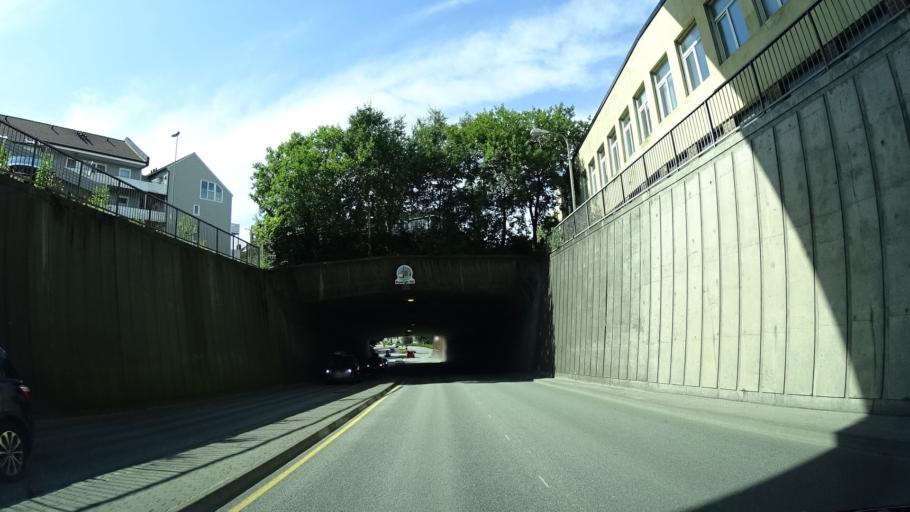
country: NO
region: Rogaland
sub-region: Stavanger
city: Stavanger
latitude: 58.9698
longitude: 5.7487
